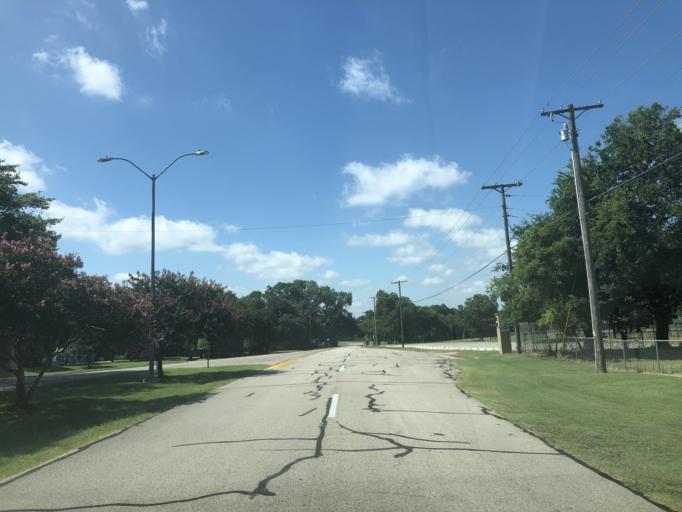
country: US
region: Texas
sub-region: Dallas County
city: Duncanville
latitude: 32.6580
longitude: -96.9172
